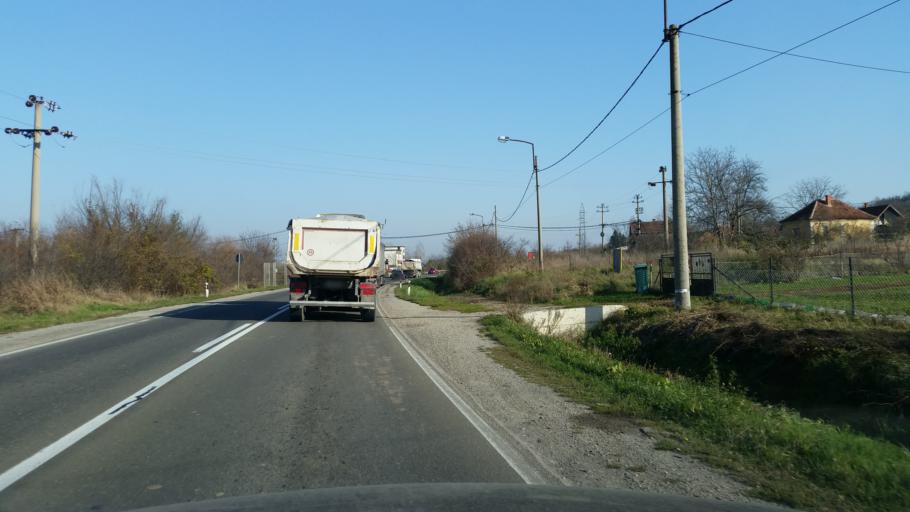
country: RS
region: Central Serbia
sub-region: Kolubarski Okrug
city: Lajkovac
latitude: 44.3685
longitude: 20.2063
